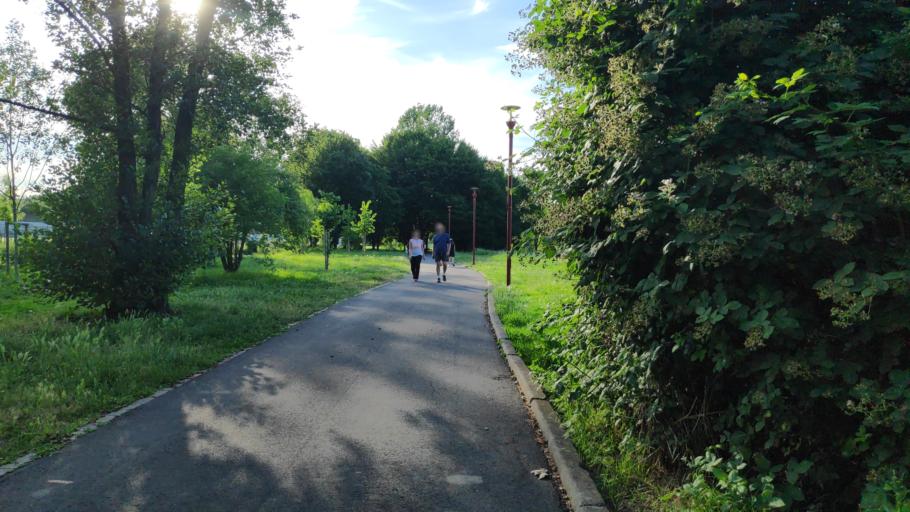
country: IT
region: Lombardy
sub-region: Citta metropolitana di Milano
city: Basiglio
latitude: 45.3560
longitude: 9.1561
